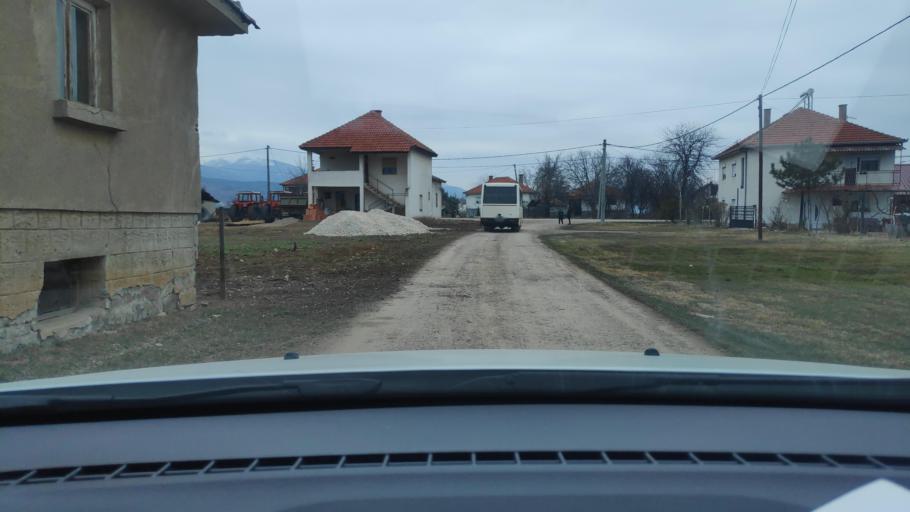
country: MK
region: Opstina Lipkovo
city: Matejche
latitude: 42.0860
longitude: 21.6209
